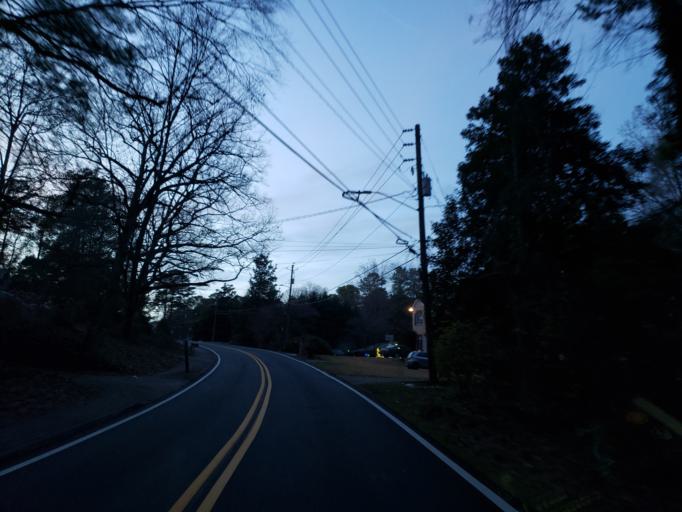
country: US
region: Georgia
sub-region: DeKalb County
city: Scottdale
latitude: 33.8263
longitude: -84.2740
